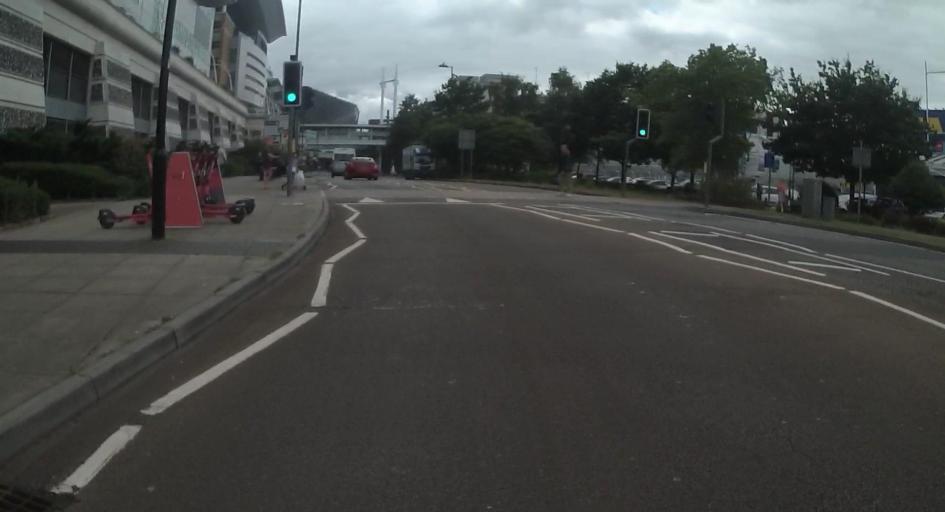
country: GB
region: England
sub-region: Southampton
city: Southampton
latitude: 50.9044
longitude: -1.4087
